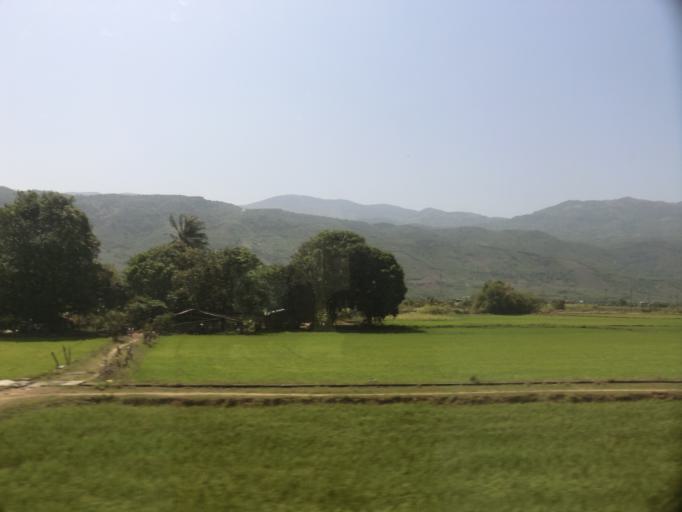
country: VN
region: Khanh Hoa
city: Cam Ranh
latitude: 11.7925
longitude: 109.0884
